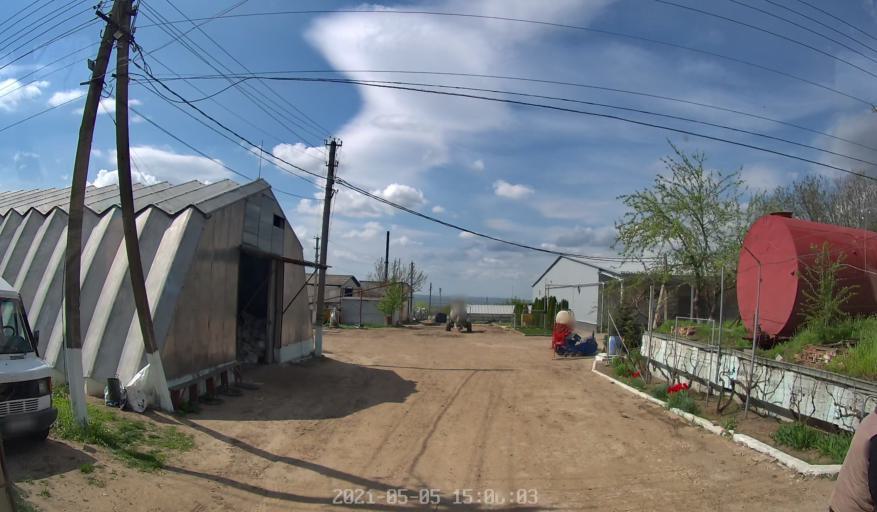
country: MD
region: Chisinau
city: Vadul lui Voda
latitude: 47.0997
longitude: 29.1893
